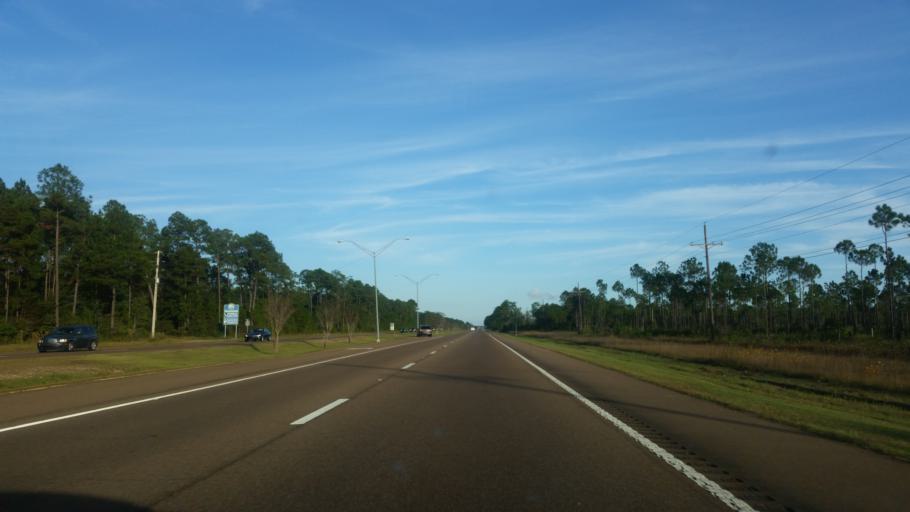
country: US
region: Mississippi
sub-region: Jackson County
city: Gulf Park Estates
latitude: 30.3984
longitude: -88.6950
